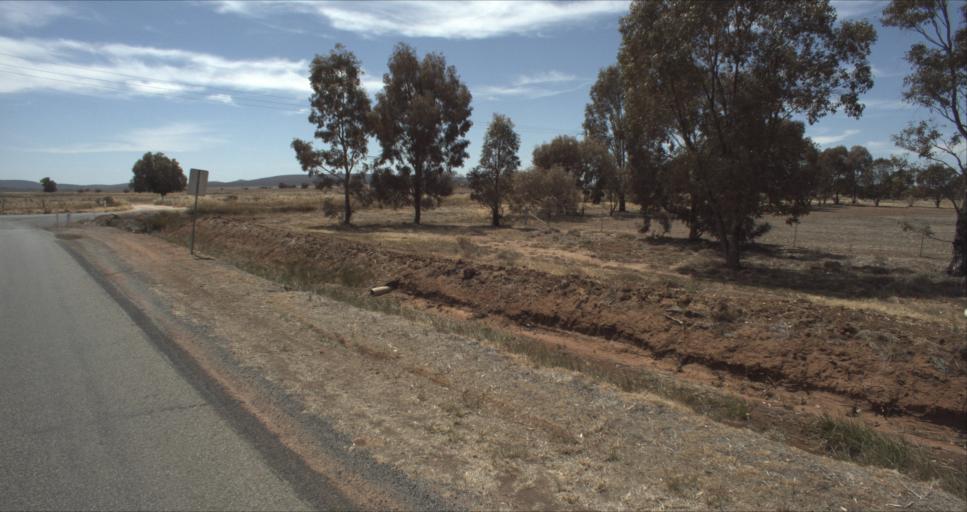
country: AU
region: New South Wales
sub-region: Leeton
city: Leeton
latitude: -34.5575
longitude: 146.4535
